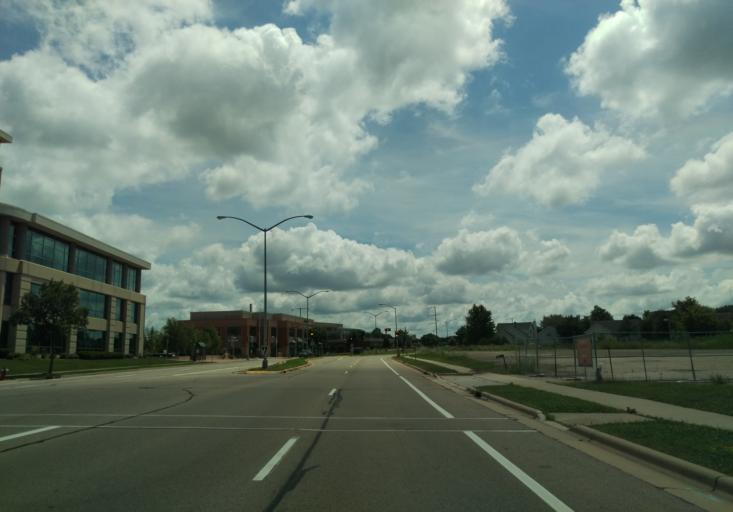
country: US
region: Wisconsin
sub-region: Dane County
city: Middleton
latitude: 43.0728
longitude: -89.5260
